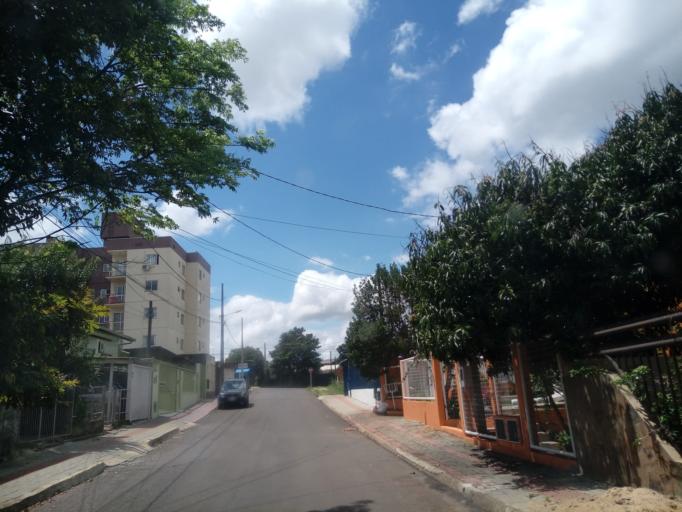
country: BR
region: Santa Catarina
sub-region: Chapeco
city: Chapeco
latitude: -27.0980
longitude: -52.6390
